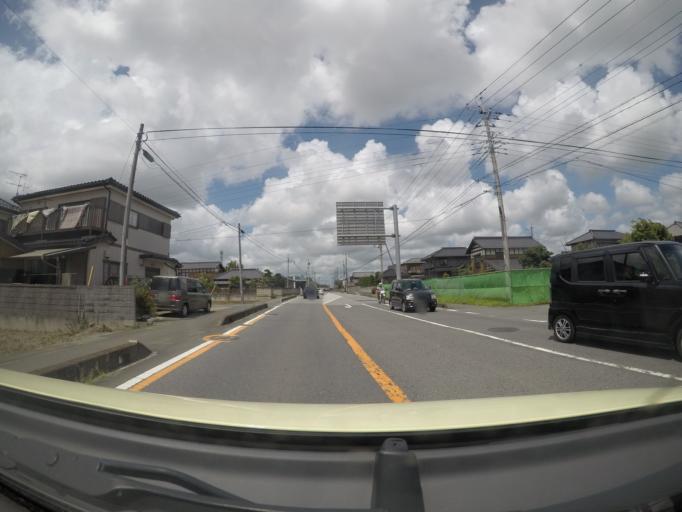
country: JP
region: Ibaraki
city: Mitsukaido
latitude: 36.0361
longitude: 139.9875
